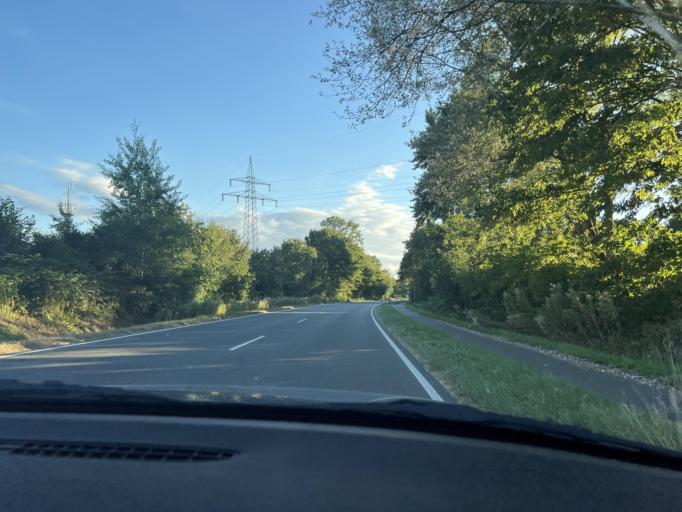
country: DE
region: Schleswig-Holstein
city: Norderheistedt
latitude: 54.2428
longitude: 9.1635
